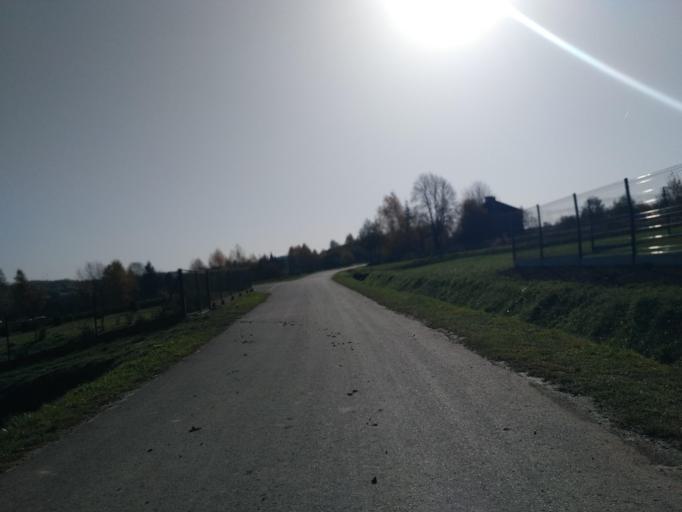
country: PL
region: Subcarpathian Voivodeship
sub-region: Powiat rzeszowski
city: Blazowa
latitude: 49.8655
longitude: 22.1232
